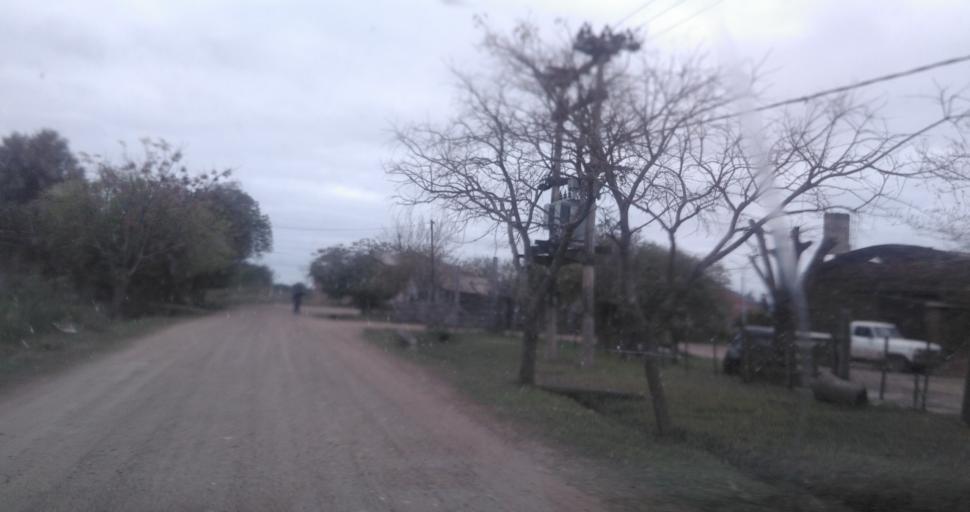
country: AR
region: Chaco
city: Fontana
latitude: -27.4340
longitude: -59.0265
